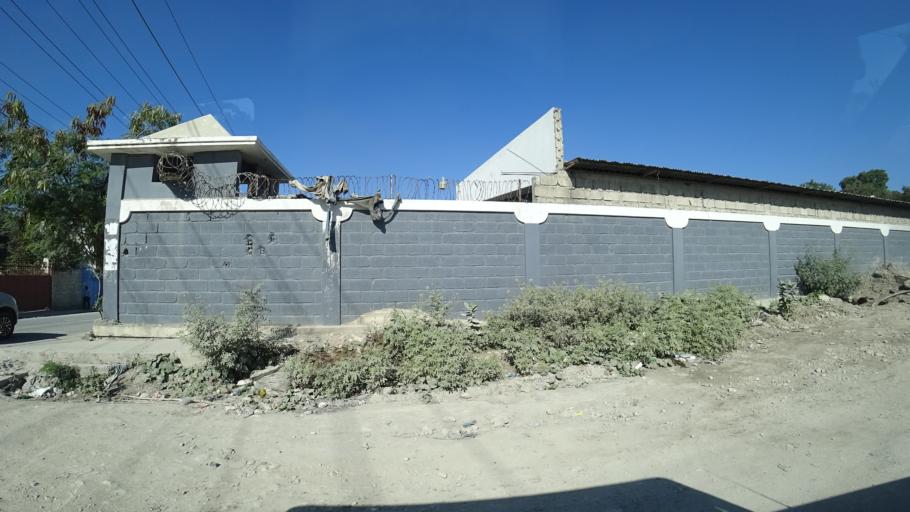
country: HT
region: Ouest
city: Delmas 73
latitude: 18.5597
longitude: -72.3035
